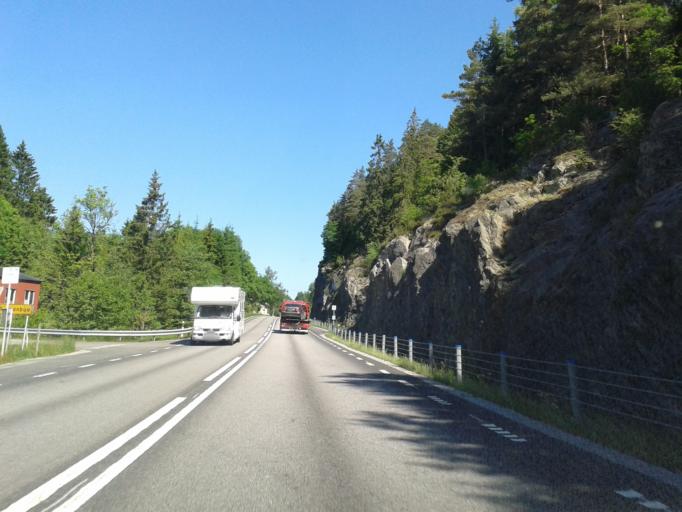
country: SE
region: Vaestra Goetaland
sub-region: Orust
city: Henan
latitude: 58.2250
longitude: 11.6861
